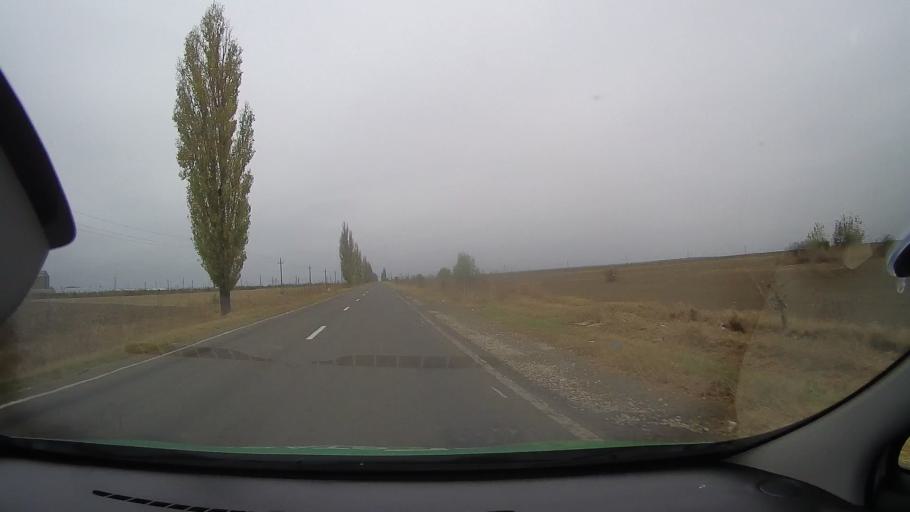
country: RO
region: Ialomita
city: Tandarei
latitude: 44.6570
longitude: 27.6508
